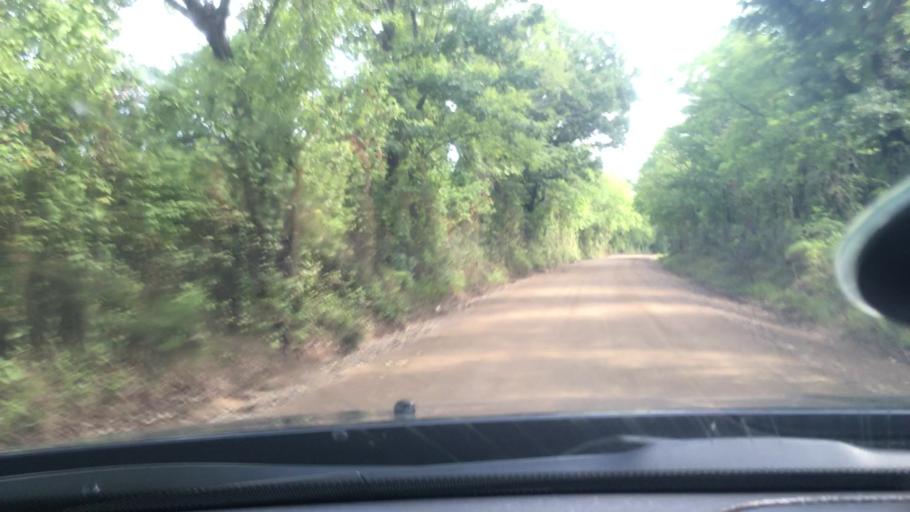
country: US
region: Oklahoma
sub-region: Atoka County
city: Atoka
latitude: 34.4522
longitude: -96.0665
